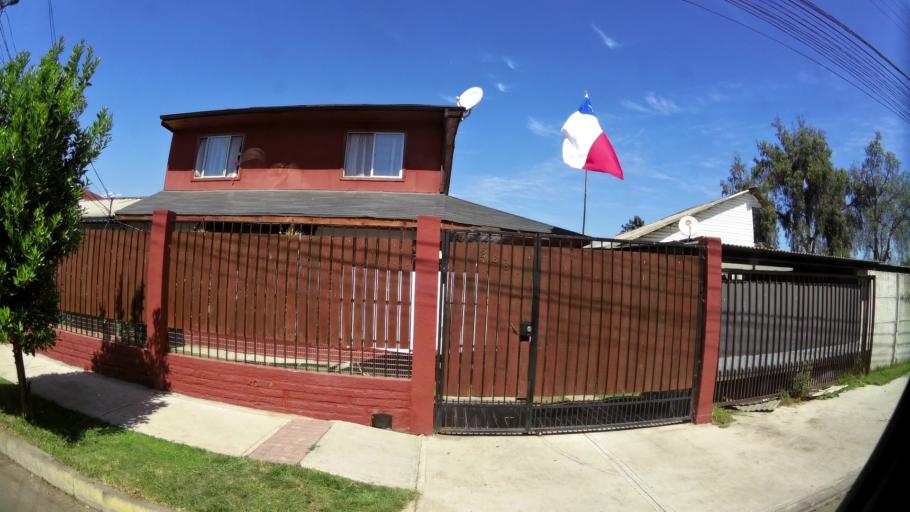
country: CL
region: Santiago Metropolitan
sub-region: Provincia de Talagante
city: Talagante
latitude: -33.6494
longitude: -70.9283
